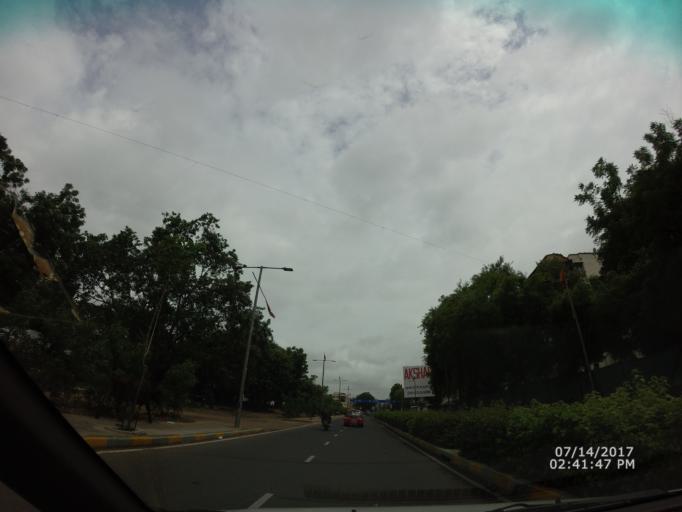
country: IN
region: Gujarat
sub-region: Ahmadabad
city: Ahmedabad
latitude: 23.0643
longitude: 72.5964
